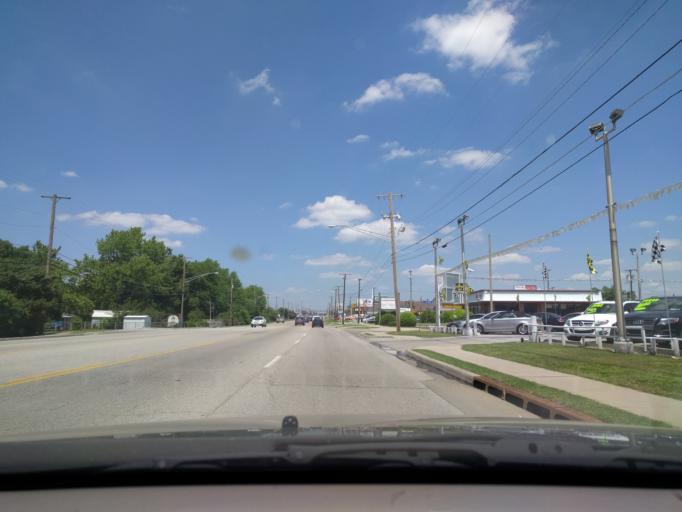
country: US
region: Oklahoma
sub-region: Tulsa County
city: Broken Arrow
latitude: 36.0626
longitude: -95.7974
